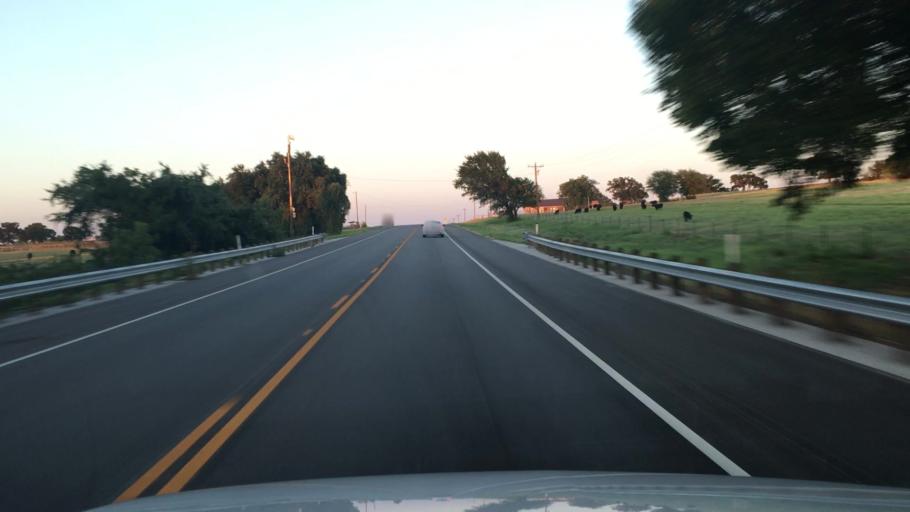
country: US
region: Texas
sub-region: Somervell County
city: Glen Rose
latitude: 32.1902
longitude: -97.8558
